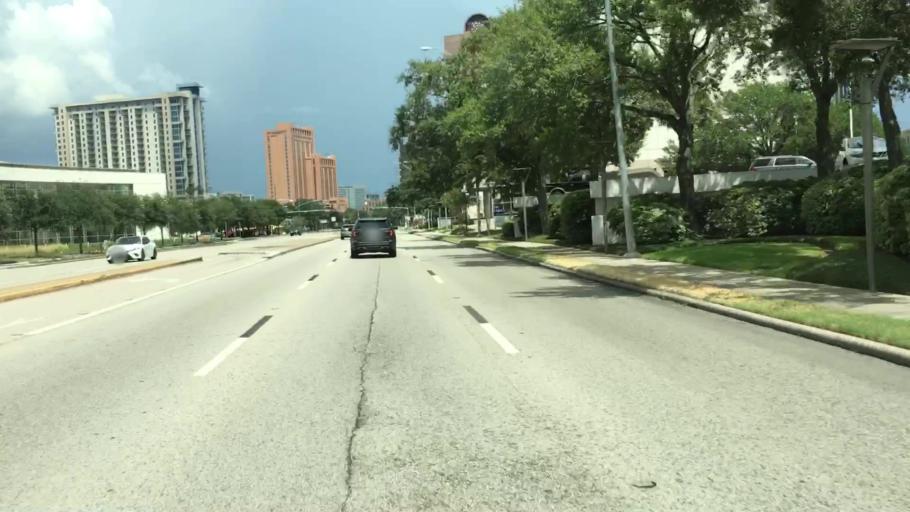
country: US
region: Texas
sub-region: Harris County
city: Bellaire
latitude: 29.7384
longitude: -95.4729
